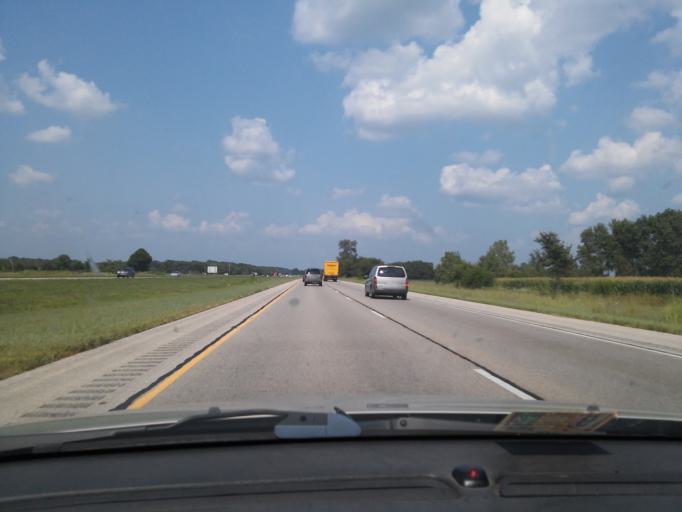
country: US
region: Illinois
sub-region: Logan County
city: Atlanta
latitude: 40.3337
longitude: -89.1460
